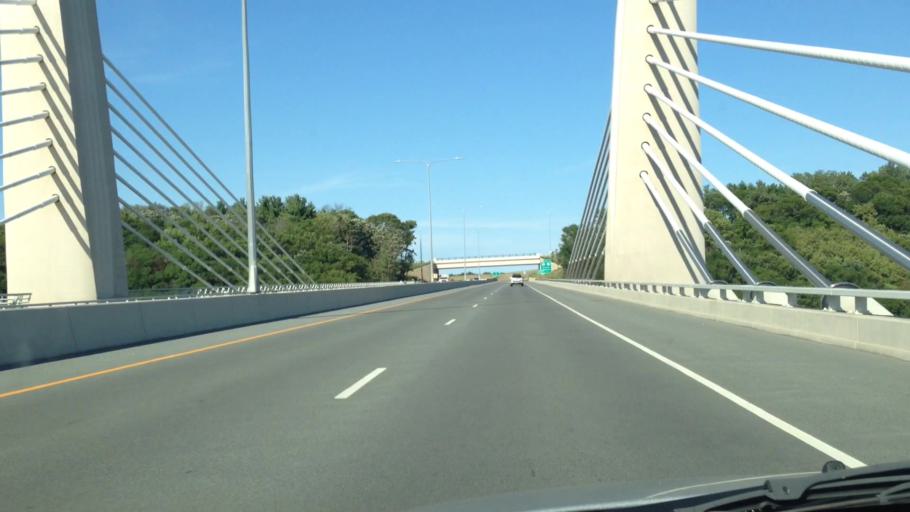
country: US
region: Minnesota
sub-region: Washington County
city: Oak Park Heights
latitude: 45.0437
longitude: -92.7815
